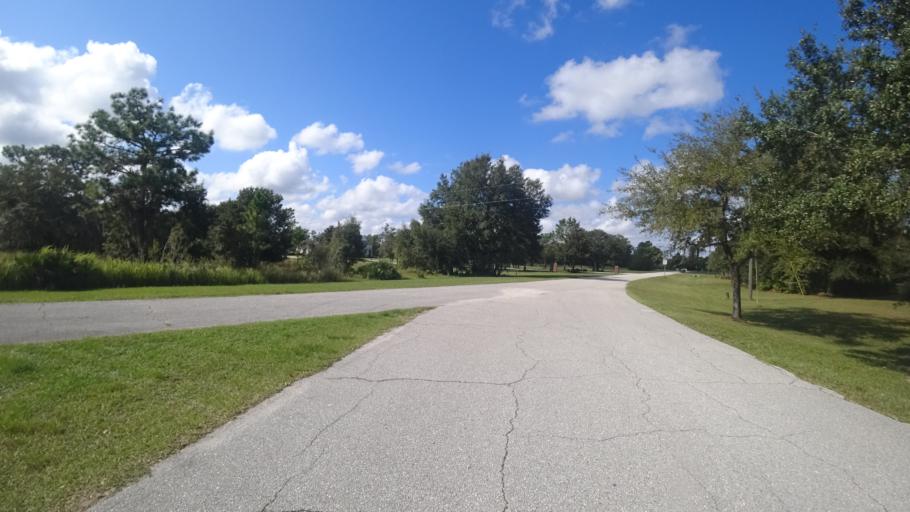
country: US
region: Florida
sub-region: Sarasota County
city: The Meadows
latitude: 27.3983
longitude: -82.3221
